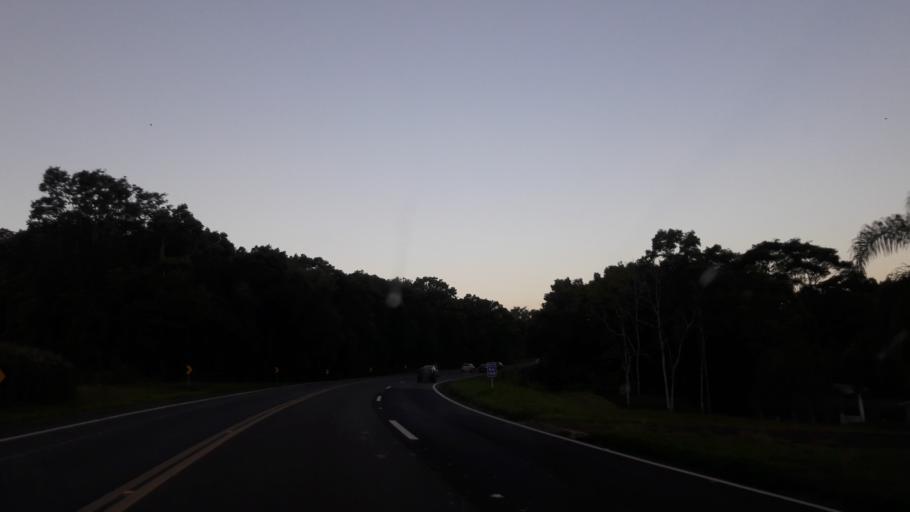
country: BR
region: Parana
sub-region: Palmeira
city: Palmeira
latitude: -25.4655
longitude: -50.2716
